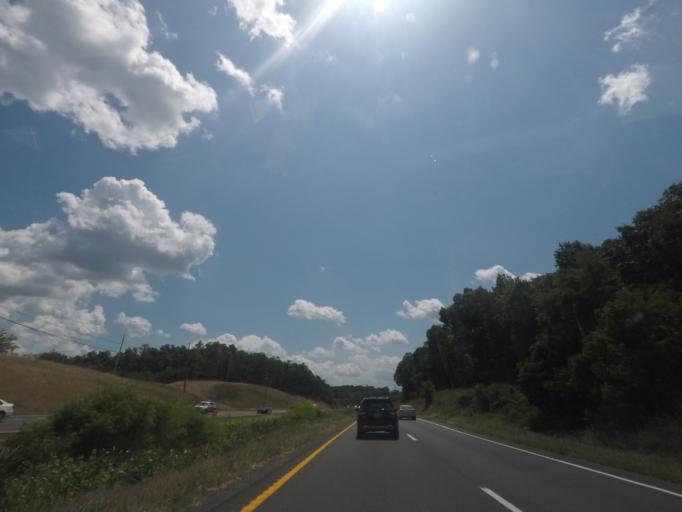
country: US
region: Virginia
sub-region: City of Winchester
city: Winchester
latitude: 39.1393
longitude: -78.1234
